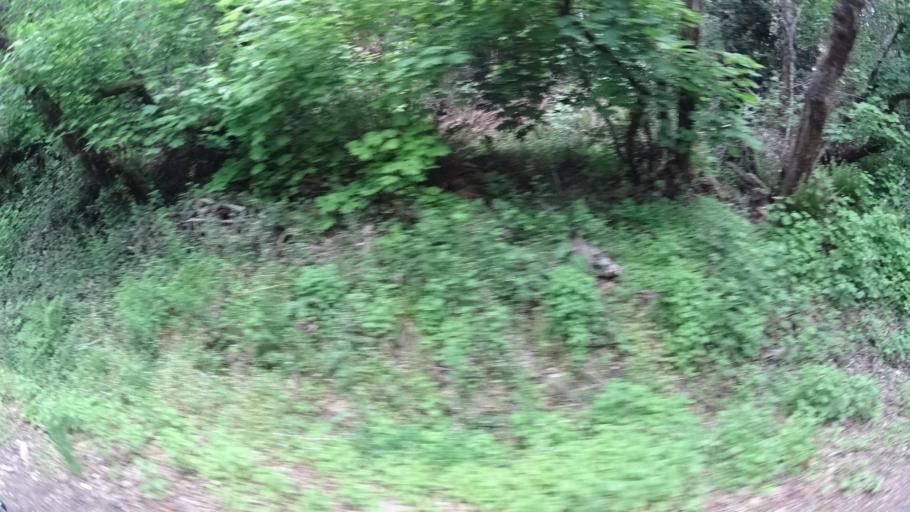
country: US
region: California
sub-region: Humboldt County
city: Willow Creek
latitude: 41.2028
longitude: -123.7559
